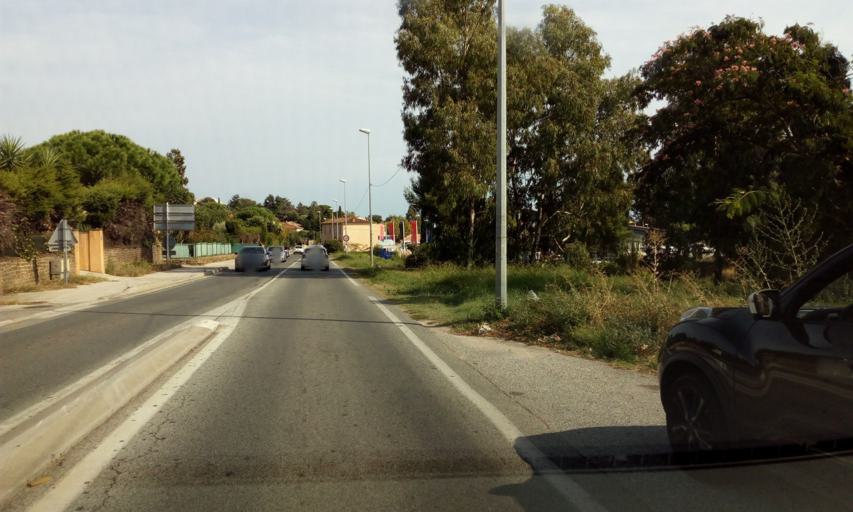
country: FR
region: Provence-Alpes-Cote d'Azur
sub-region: Departement du Var
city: Bormes-les-Mimosas
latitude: 43.1422
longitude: 6.3473
